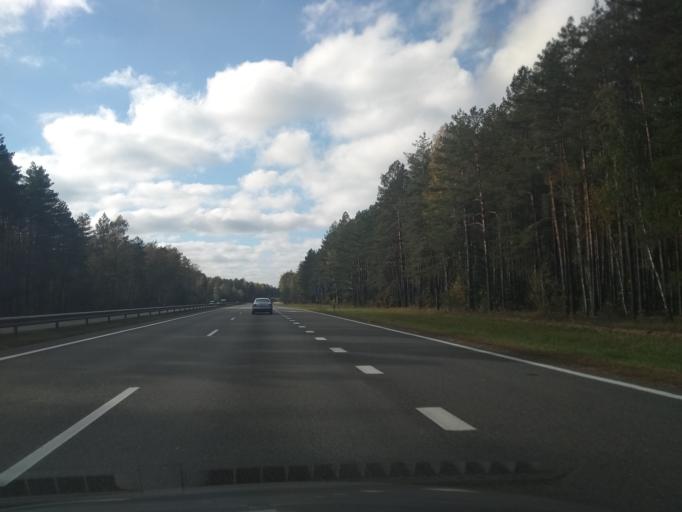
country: BY
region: Minsk
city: Enyerhyetykaw
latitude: 53.5550
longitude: 26.9687
